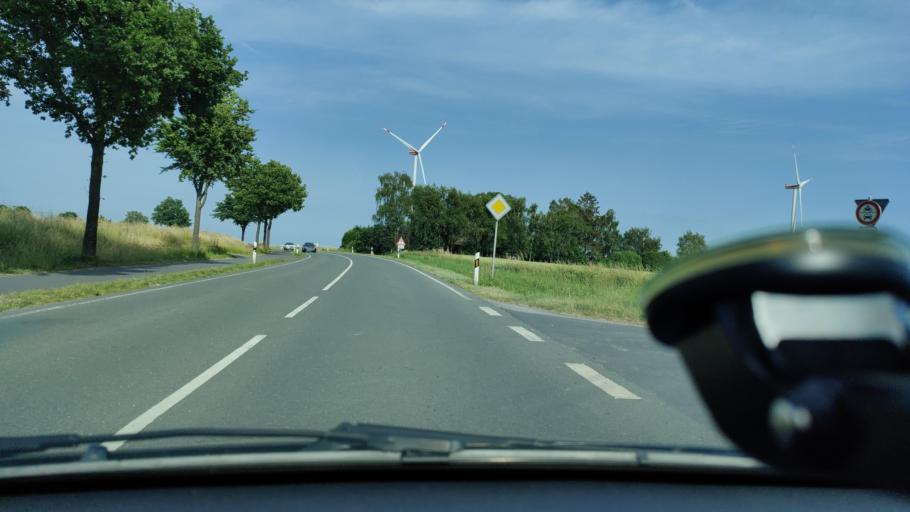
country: DE
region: North Rhine-Westphalia
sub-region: Regierungsbezirk Munster
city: Legden
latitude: 52.0110
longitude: 7.1629
